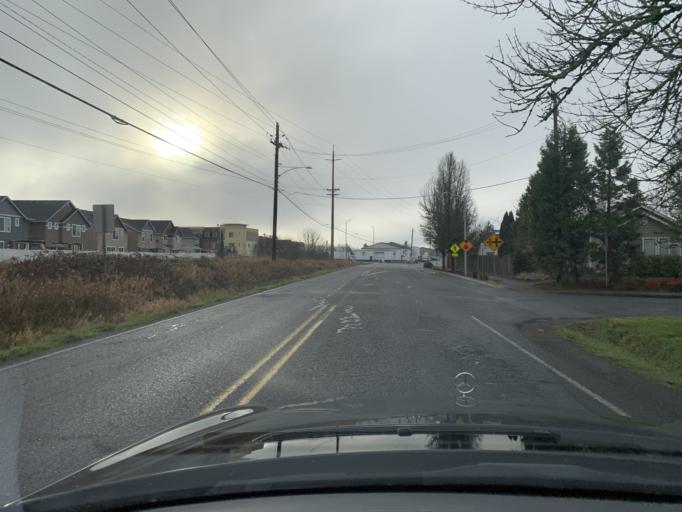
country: US
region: Washington
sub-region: Clark County
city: Battle Ground
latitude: 45.7766
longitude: -122.5272
